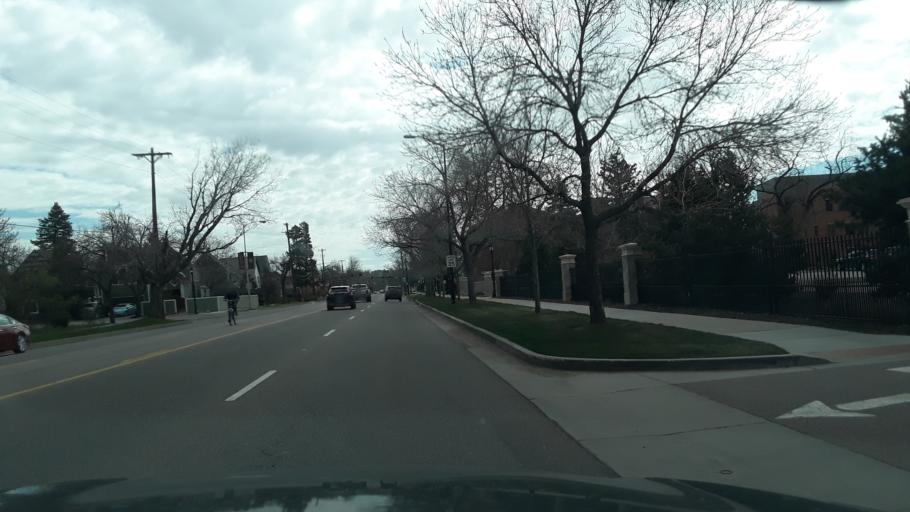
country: US
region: Colorado
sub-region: El Paso County
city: Colorado Springs
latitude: 38.8506
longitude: -104.8236
